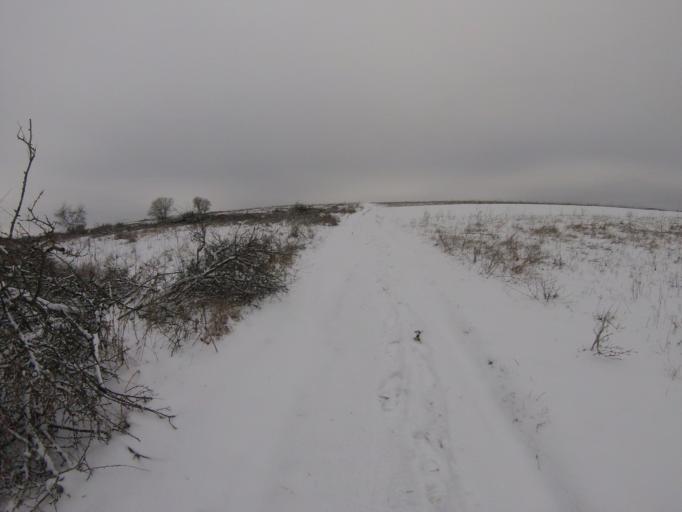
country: HU
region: Borsod-Abauj-Zemplen
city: Rudabanya
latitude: 48.4433
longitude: 20.6185
